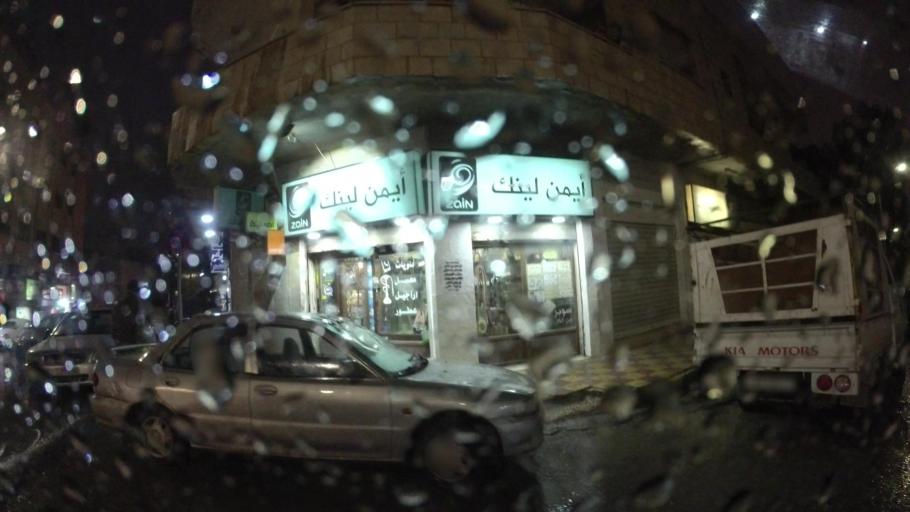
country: JO
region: Amman
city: Al Jubayhah
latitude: 32.0239
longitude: 35.8490
